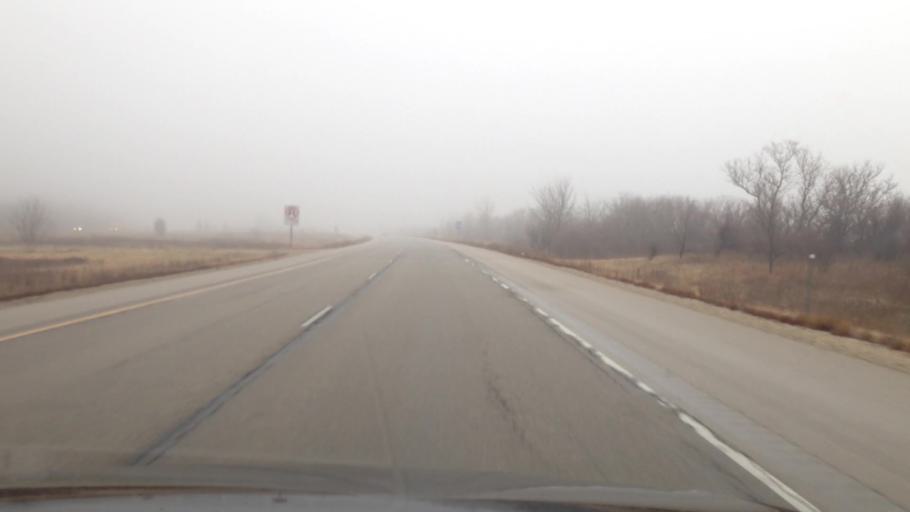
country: US
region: Wisconsin
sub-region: Walworth County
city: East Troy
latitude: 42.7527
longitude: -88.4383
